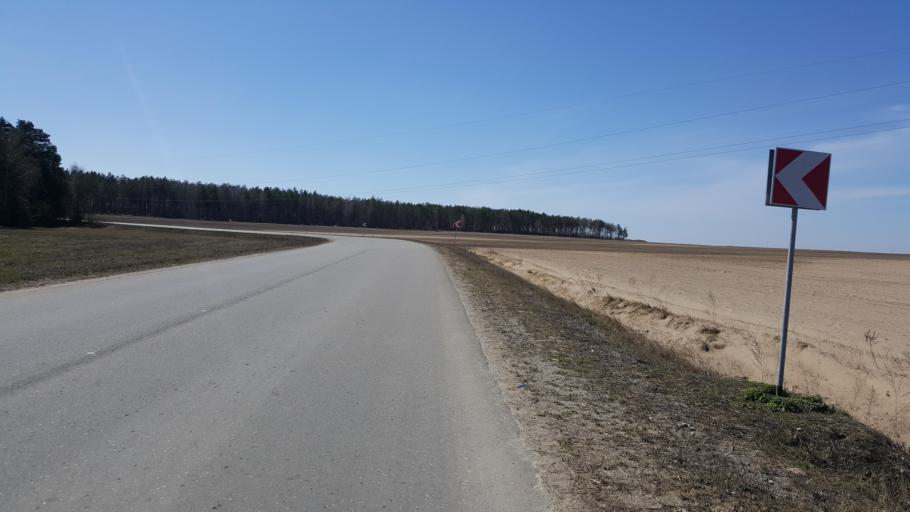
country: BY
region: Brest
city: Kamyanyets
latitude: 52.2832
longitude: 23.8501
